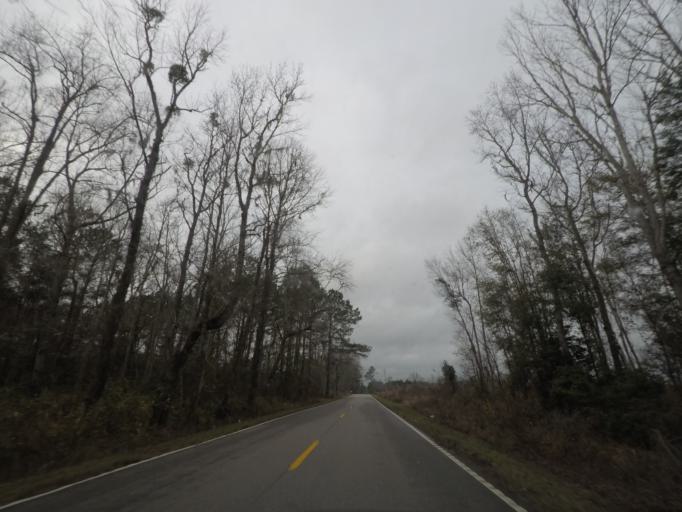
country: US
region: South Carolina
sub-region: Colleton County
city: Walterboro
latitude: 32.8831
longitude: -80.5035
